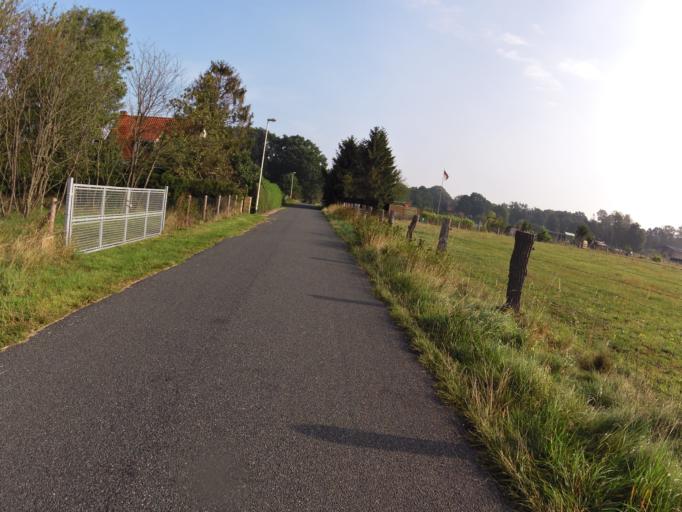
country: DE
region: Lower Saxony
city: Verden
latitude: 52.9393
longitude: 9.2267
